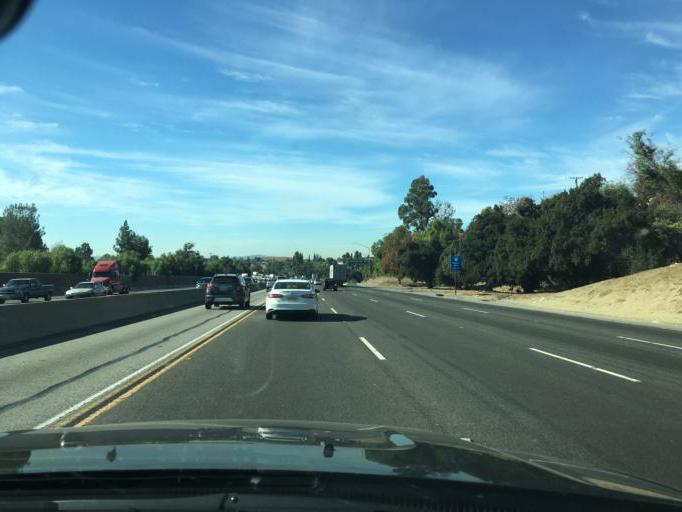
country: US
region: California
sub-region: Los Angeles County
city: Diamond Bar
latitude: 34.0262
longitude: -117.8043
